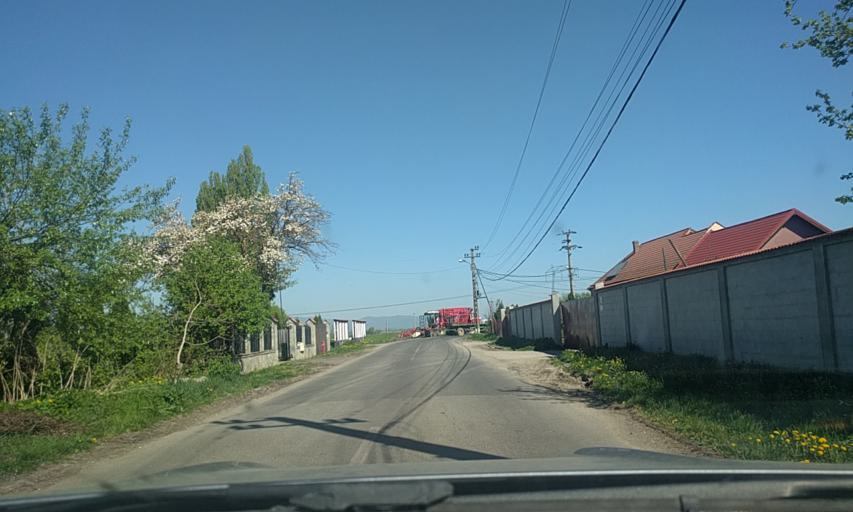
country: RO
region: Brasov
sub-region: Comuna Bod
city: Colonia Bod
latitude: 45.7109
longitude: 25.5684
